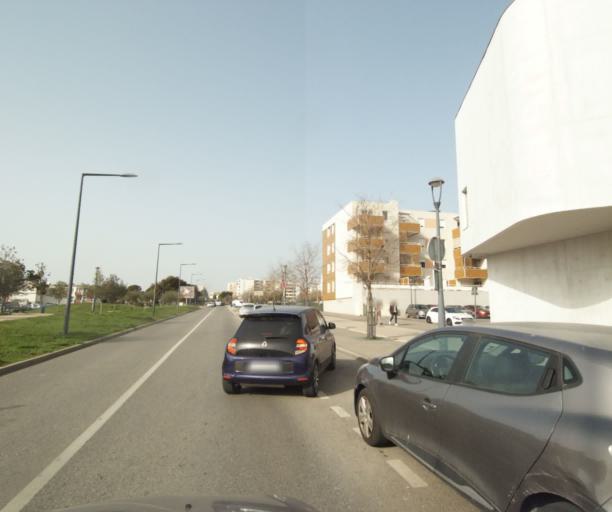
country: FR
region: Provence-Alpes-Cote d'Azur
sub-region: Departement des Bouches-du-Rhone
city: Vitrolles
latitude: 43.4432
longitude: 5.2522
